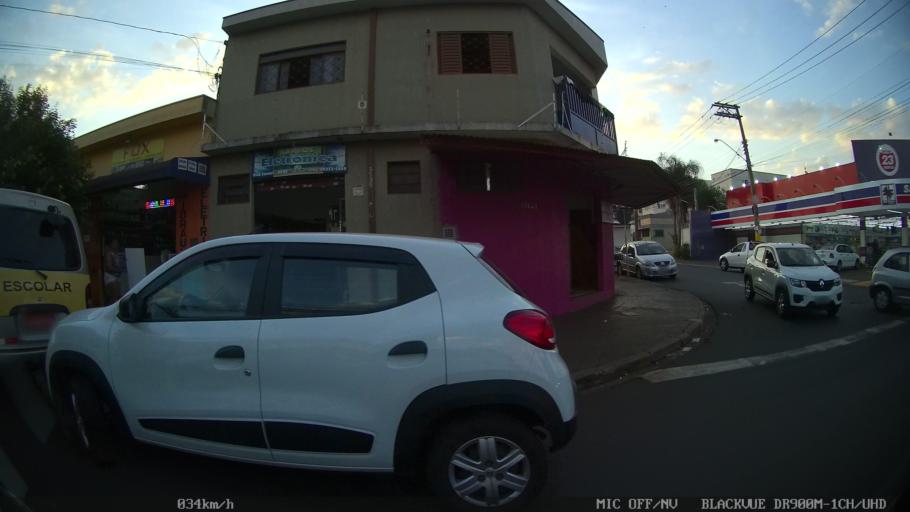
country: BR
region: Sao Paulo
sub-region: Ribeirao Preto
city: Ribeirao Preto
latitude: -21.1310
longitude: -47.8140
